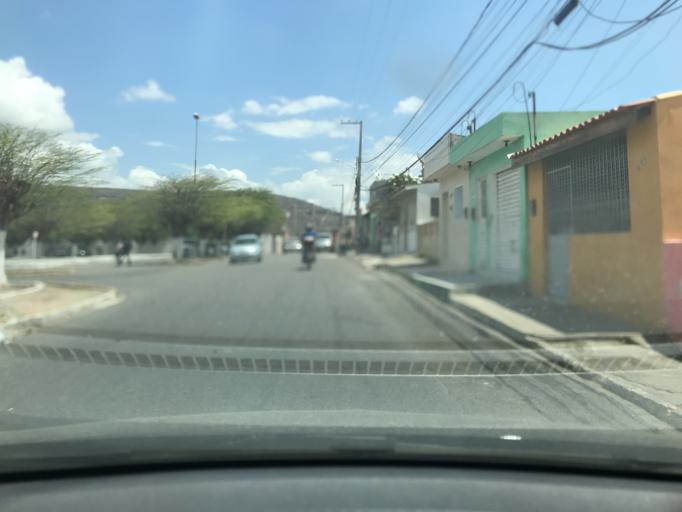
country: BR
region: Pernambuco
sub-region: Bezerros
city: Bezerros
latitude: -8.2367
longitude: -35.7454
